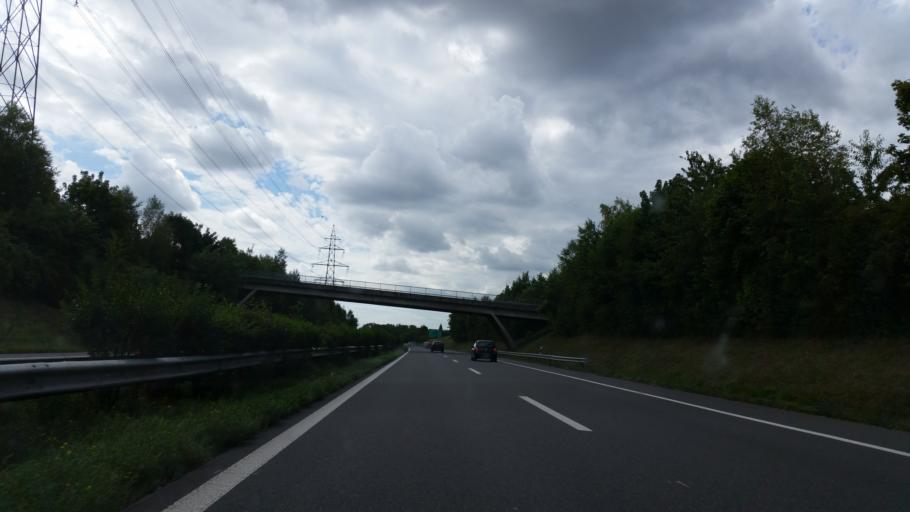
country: CH
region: Vaud
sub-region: Jura-Nord vaudois District
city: Chavornay
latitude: 46.7014
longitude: 6.5766
